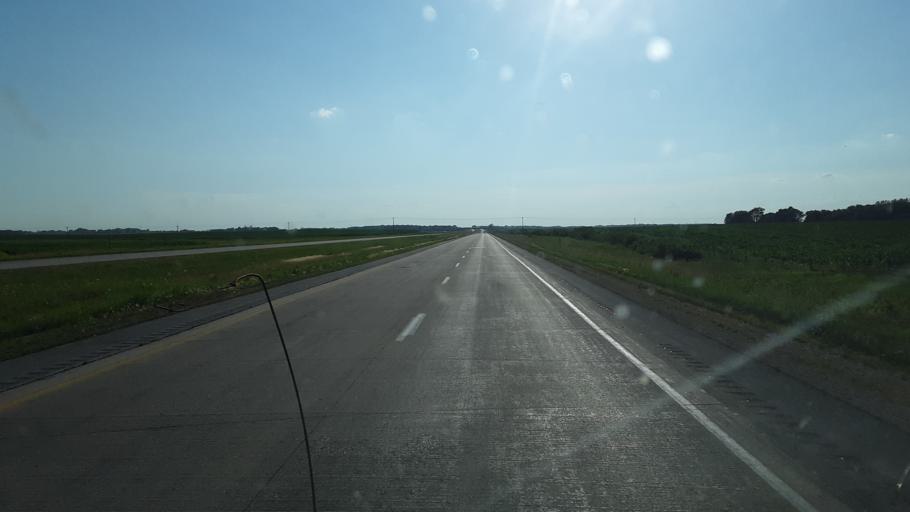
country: US
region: Iowa
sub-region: Hardin County
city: Iowa Falls
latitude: 42.4485
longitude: -93.3238
